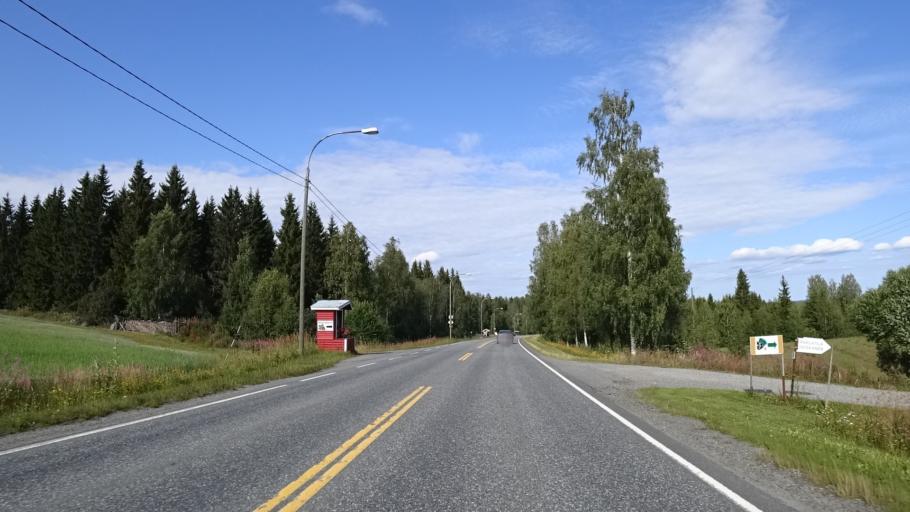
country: FI
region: North Karelia
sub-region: Joensuu
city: Eno
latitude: 62.7900
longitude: 30.0828
